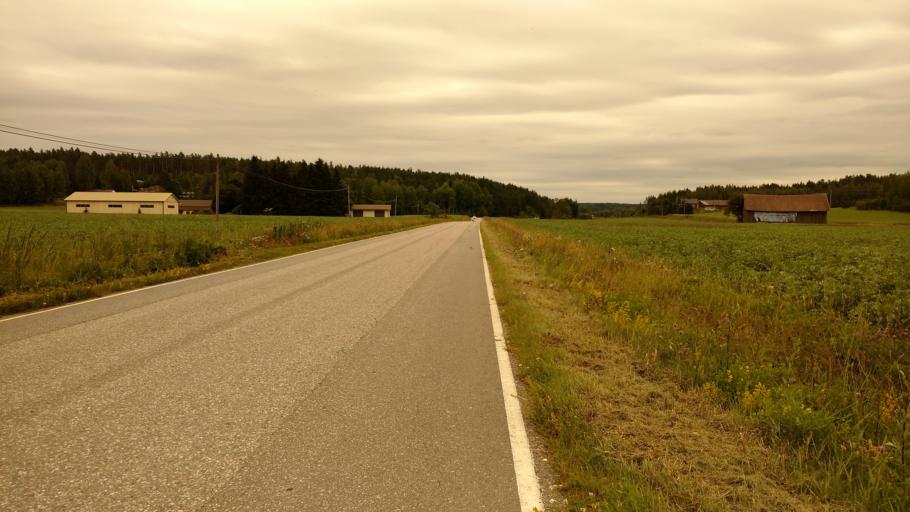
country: FI
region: Varsinais-Suomi
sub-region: Loimaa
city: Marttila
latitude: 60.4164
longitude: 22.8617
